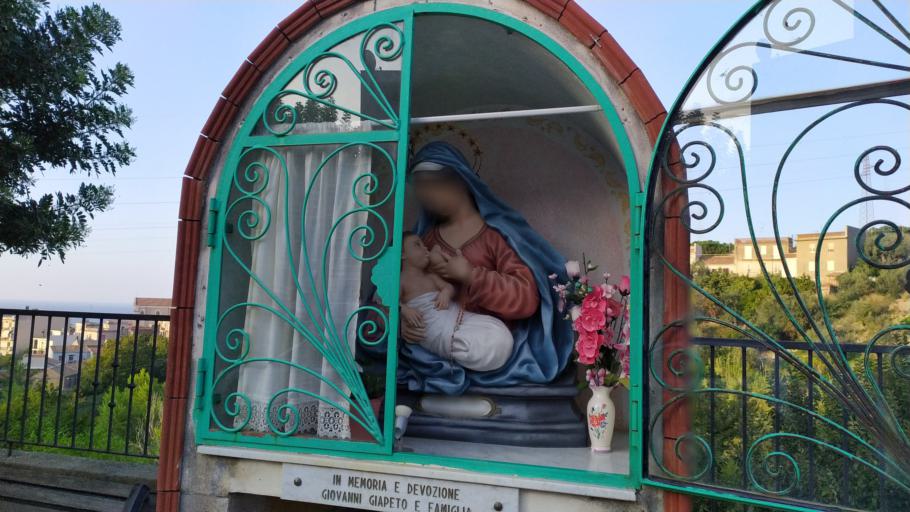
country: IT
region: Sicily
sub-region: Messina
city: Saponara Marittima
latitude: 38.2293
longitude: 15.4362
